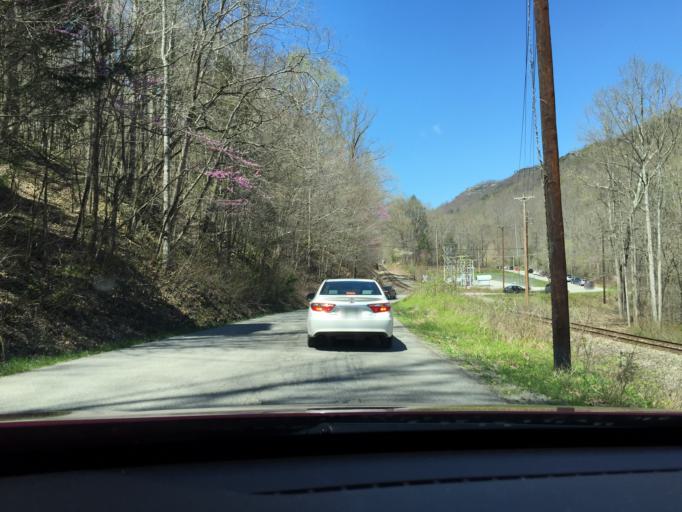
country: US
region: Tennessee
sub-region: Campbell County
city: Caryville
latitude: 36.3479
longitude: -84.2595
